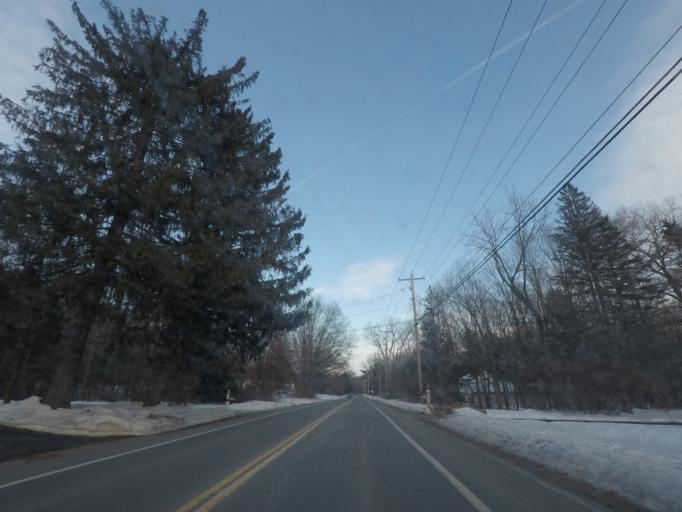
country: US
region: New York
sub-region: Schenectady County
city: Niskayuna
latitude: 42.8374
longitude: -73.8175
